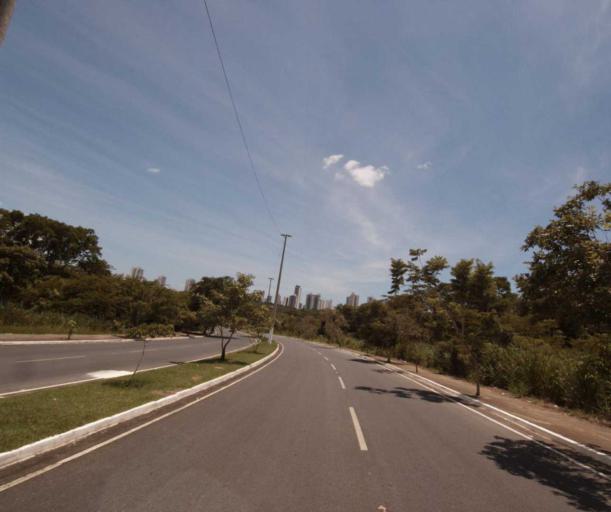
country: BR
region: Mato Grosso
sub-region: Cuiaba
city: Cuiaba
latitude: -15.5718
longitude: -56.1081
